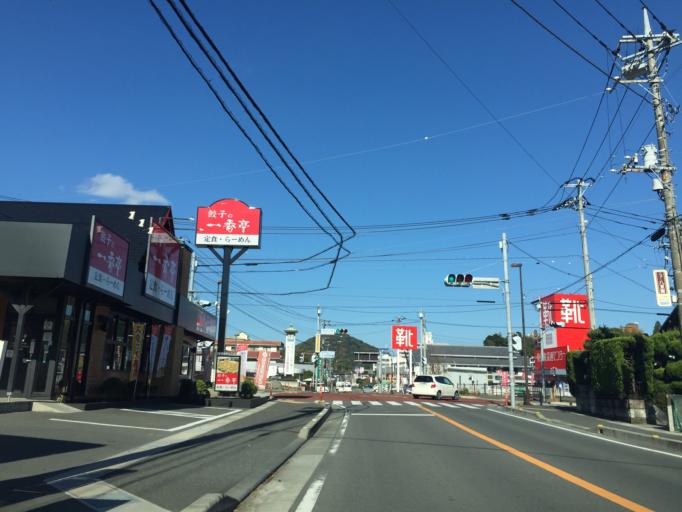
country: JP
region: Shizuoka
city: Mishima
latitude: 35.0272
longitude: 138.9297
